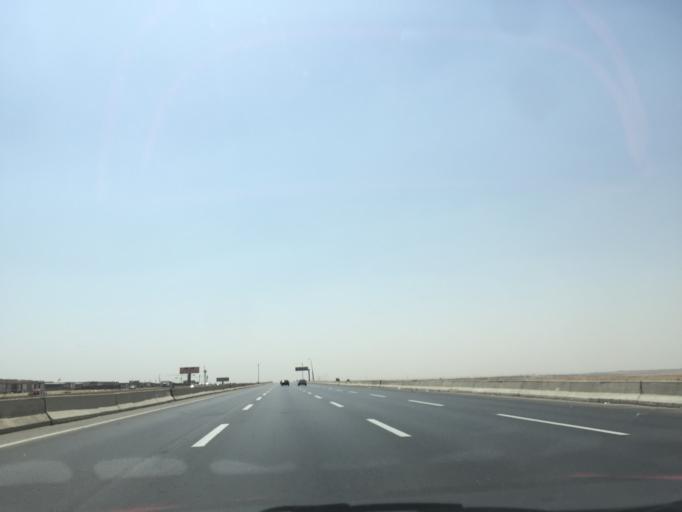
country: EG
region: Al Jizah
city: Awsim
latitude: 30.0826
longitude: 30.9568
